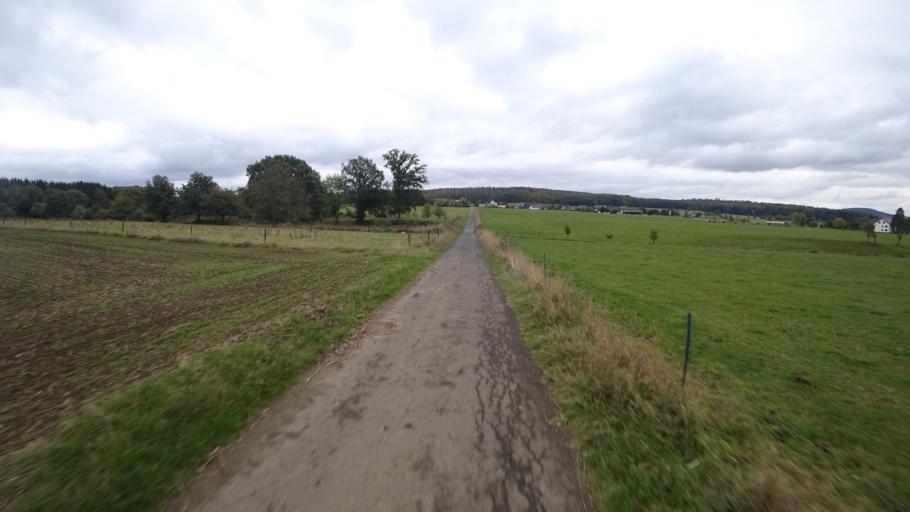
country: DE
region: Rheinland-Pfalz
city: Maxsain
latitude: 50.5498
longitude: 7.7802
